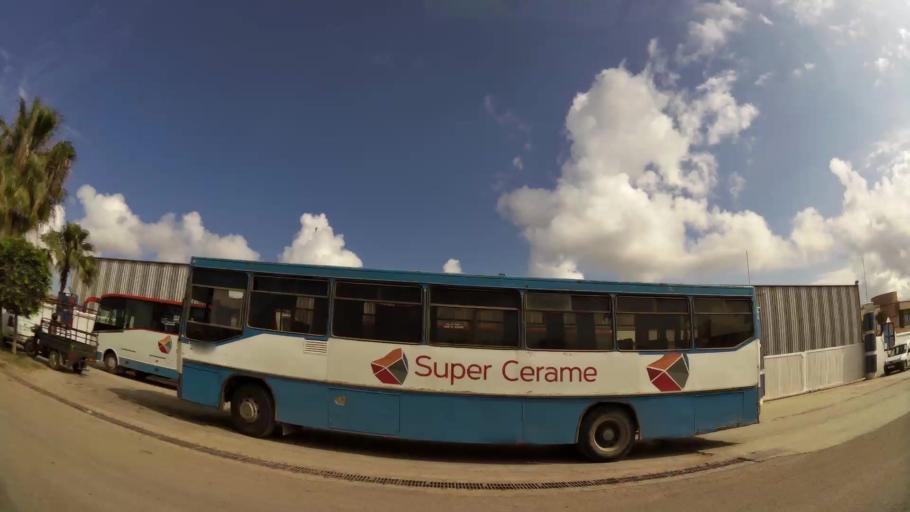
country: MA
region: Gharb-Chrarda-Beni Hssen
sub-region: Kenitra Province
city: Kenitra
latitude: 34.2786
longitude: -6.5469
